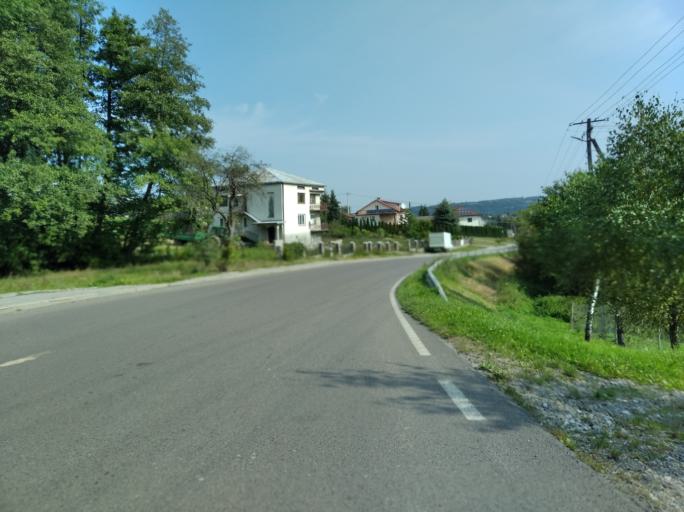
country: PL
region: Subcarpathian Voivodeship
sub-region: Powiat przeworski
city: Jawornik Polski
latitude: 49.8897
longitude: 22.2863
